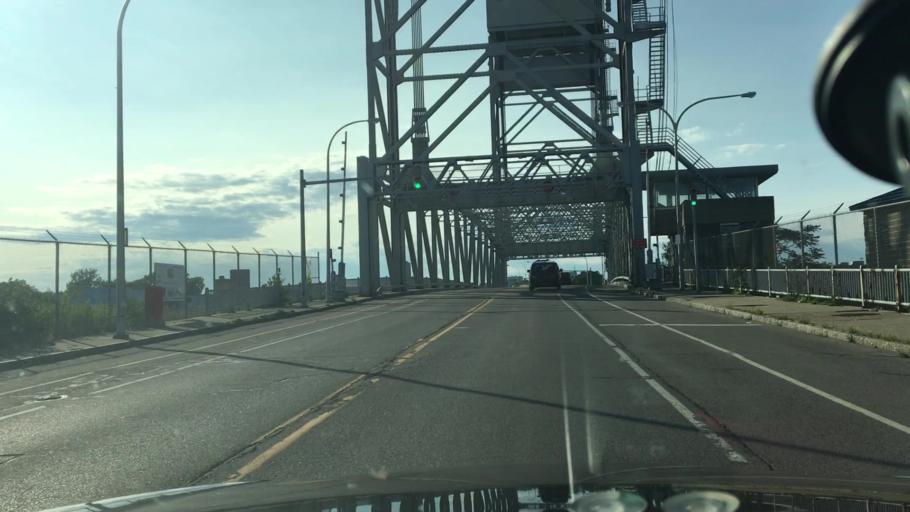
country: US
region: New York
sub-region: Erie County
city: Lackawanna
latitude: 42.8625
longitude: -78.8420
